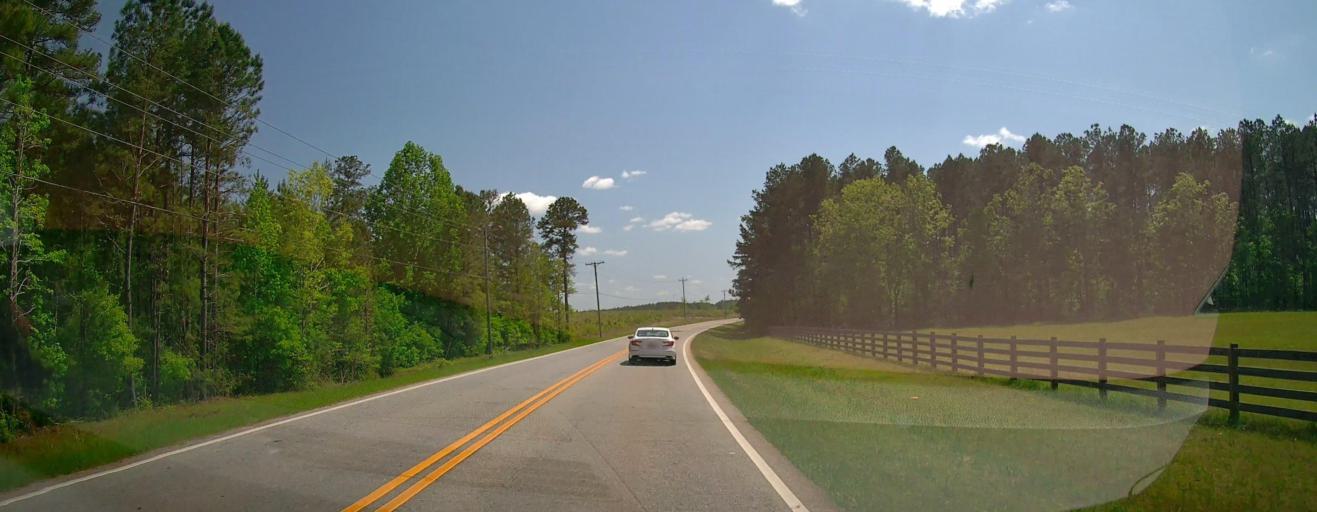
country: US
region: Georgia
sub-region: Putnam County
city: Eatonton
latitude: 33.2580
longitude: -83.3011
